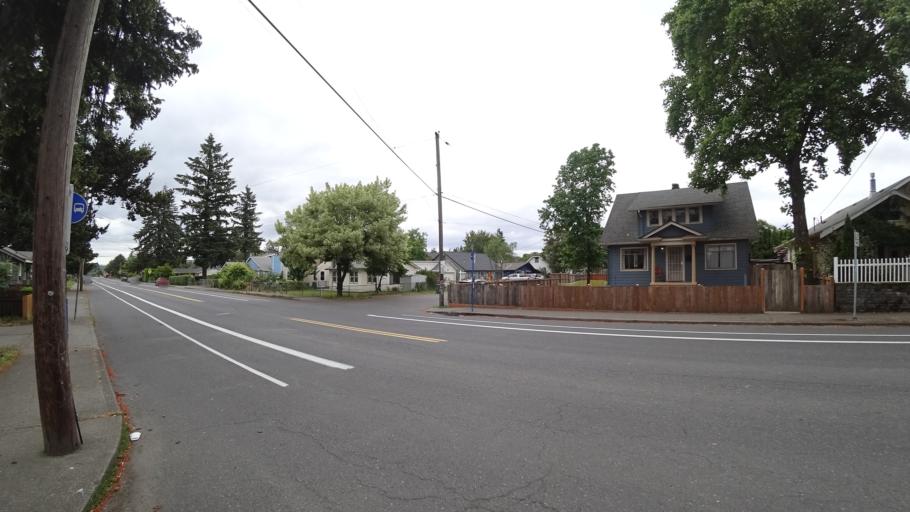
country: US
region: Oregon
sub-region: Multnomah County
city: Lents
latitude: 45.4759
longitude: -122.5868
